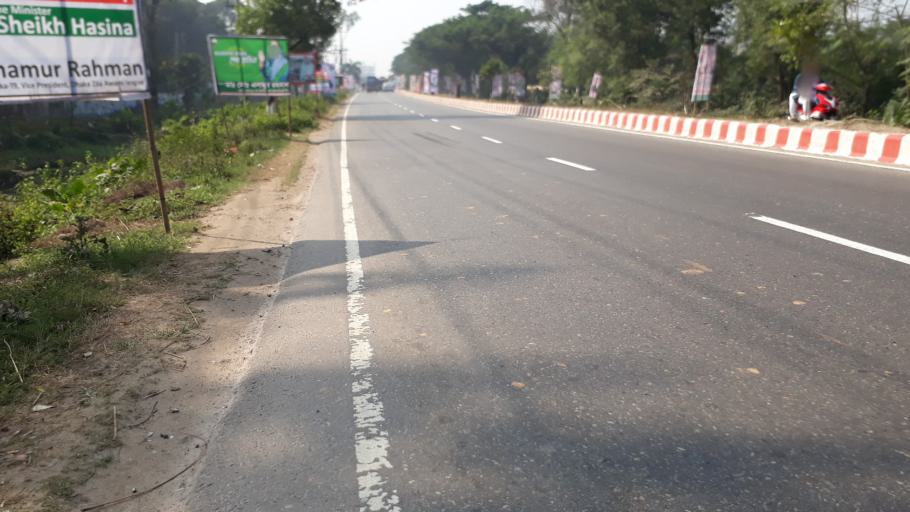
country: BD
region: Dhaka
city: Tungi
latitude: 23.8654
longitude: 90.2700
